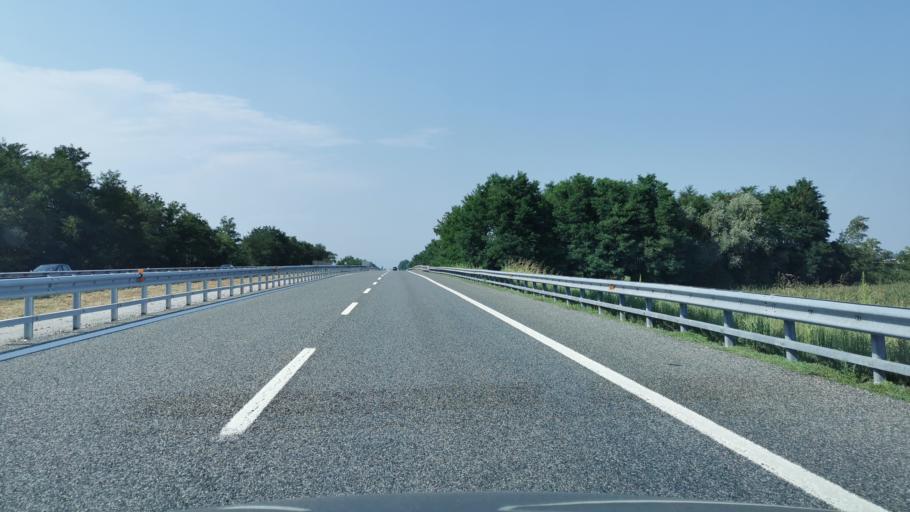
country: IT
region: Piedmont
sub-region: Provincia di Cuneo
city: Caramagna Piemonte
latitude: 44.7966
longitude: 7.7528
